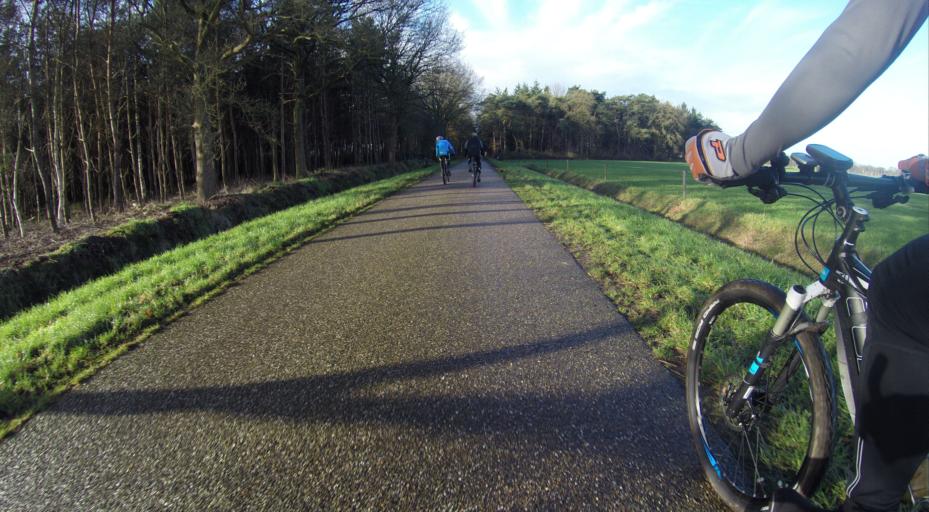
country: NL
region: Gelderland
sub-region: Gemeente Lochem
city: Laren
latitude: 52.3122
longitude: 6.3889
